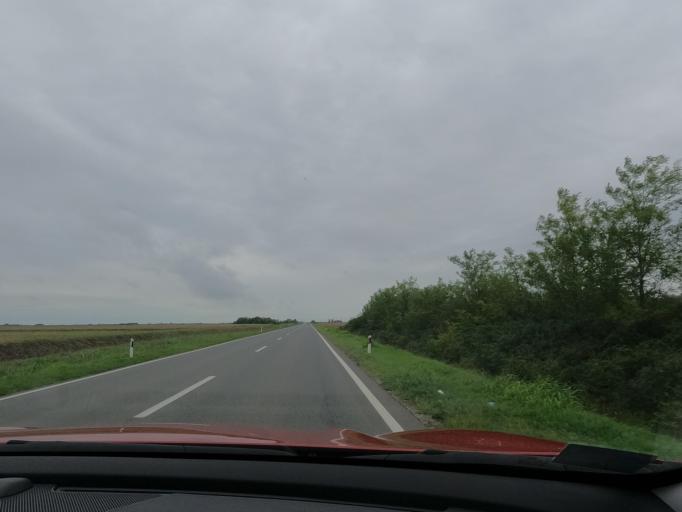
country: RS
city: Banatska Topola
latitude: 45.6995
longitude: 20.4207
